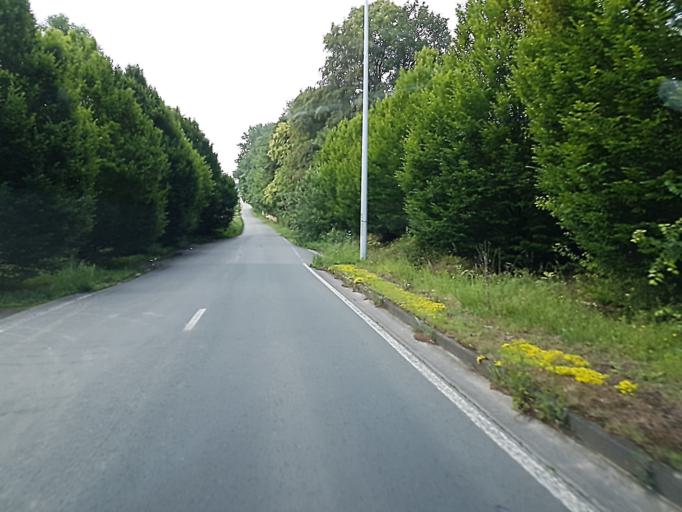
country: BE
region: Wallonia
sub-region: Province du Hainaut
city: Enghien
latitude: 50.6769
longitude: 4.0470
